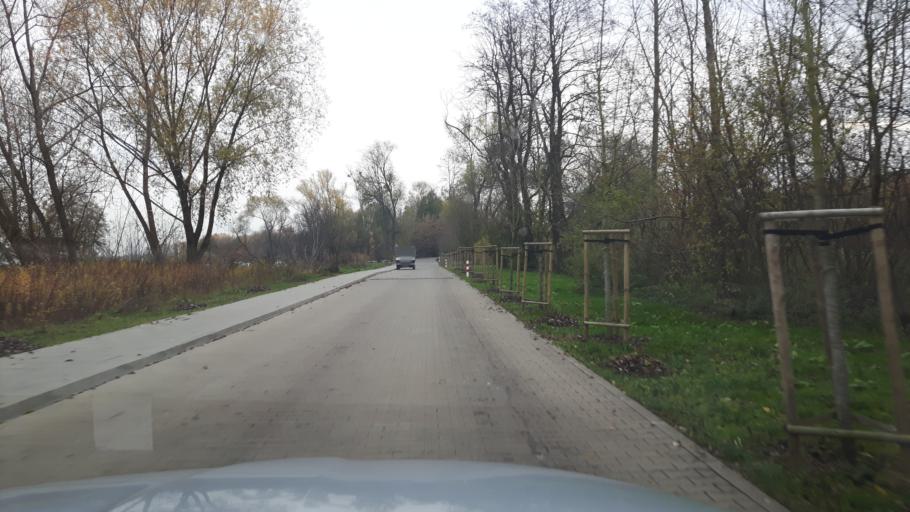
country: PL
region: Masovian Voivodeship
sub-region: Warszawa
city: Ursynow
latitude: 52.1578
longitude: 21.0616
